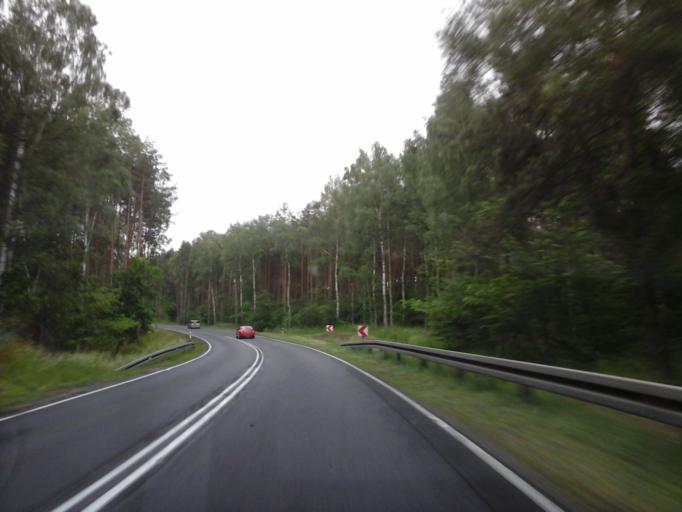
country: PL
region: West Pomeranian Voivodeship
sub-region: Powiat drawski
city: Kalisz Pomorski
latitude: 53.2896
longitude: 15.9451
